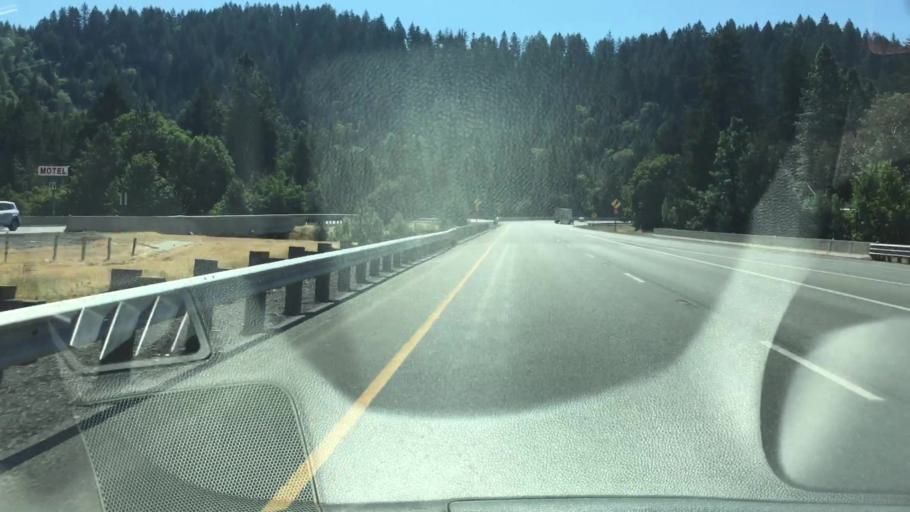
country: US
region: Oregon
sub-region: Josephine County
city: Merlin
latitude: 42.6320
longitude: -123.3824
